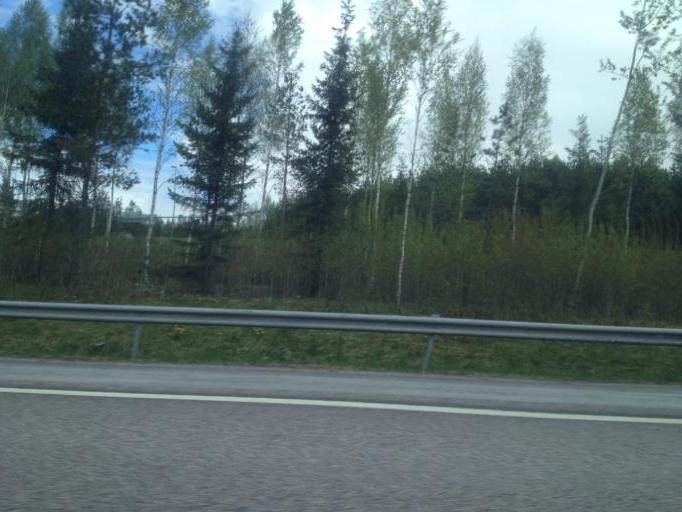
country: FI
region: Uusimaa
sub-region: Helsinki
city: Hyvinge
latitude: 60.6599
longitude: 24.7944
